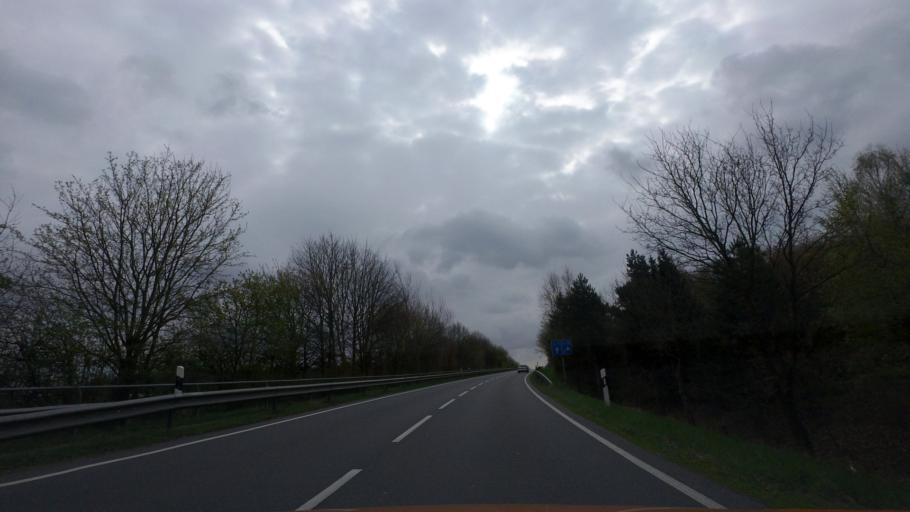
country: DE
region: Lower Saxony
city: Wardenburg
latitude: 53.0340
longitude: 8.2128
